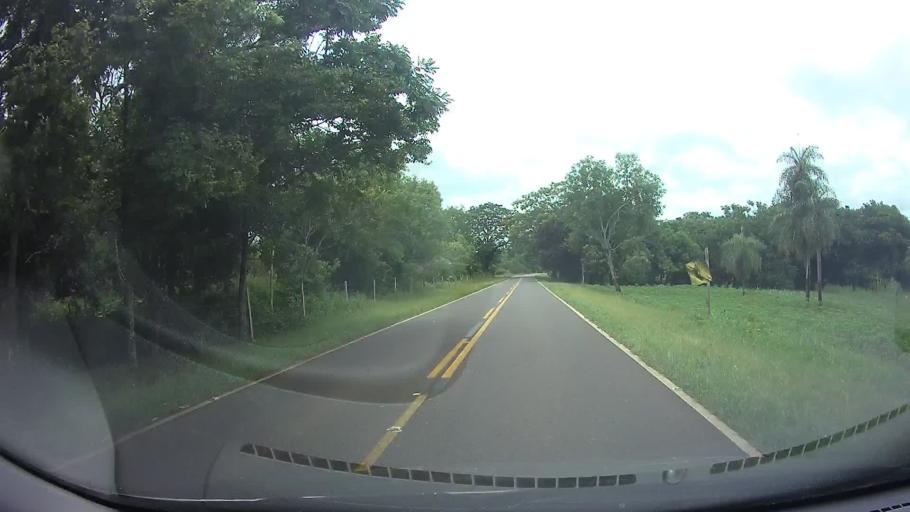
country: PY
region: Paraguari
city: Ybycui
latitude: -25.9654
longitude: -57.0837
